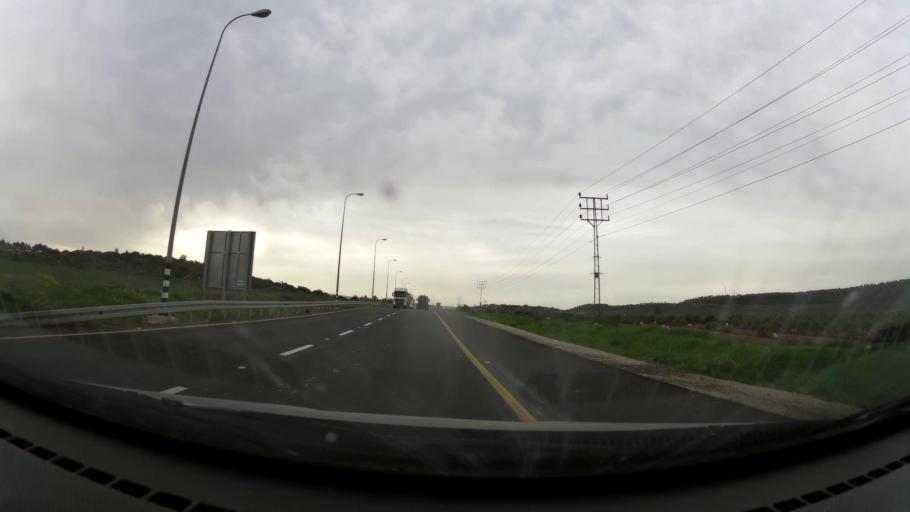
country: IL
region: Jerusalem
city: Bet Shemesh
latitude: 31.6786
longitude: 35.0047
